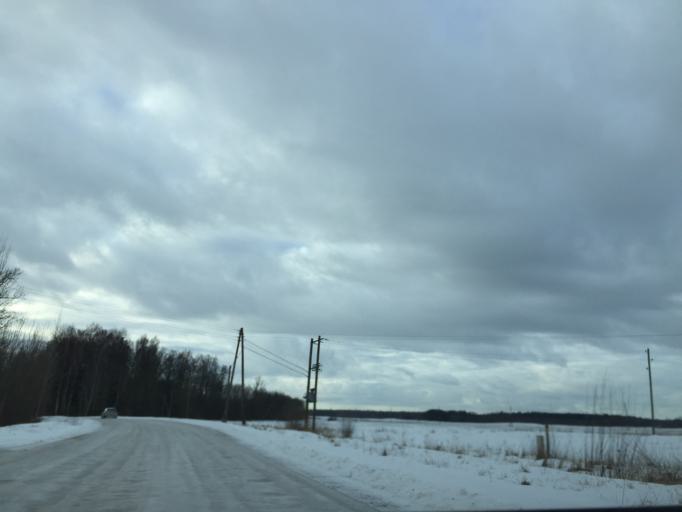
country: LV
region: Lielvarde
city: Lielvarde
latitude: 56.6002
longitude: 24.7430
